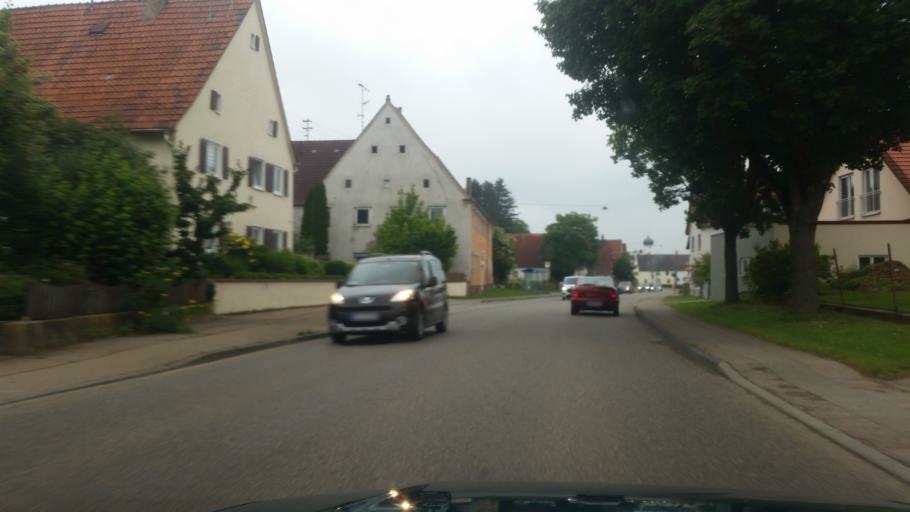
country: DE
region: Baden-Wuerttemberg
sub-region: Regierungsbezirk Stuttgart
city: Kirchheim am Ries
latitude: 48.8442
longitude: 10.3927
